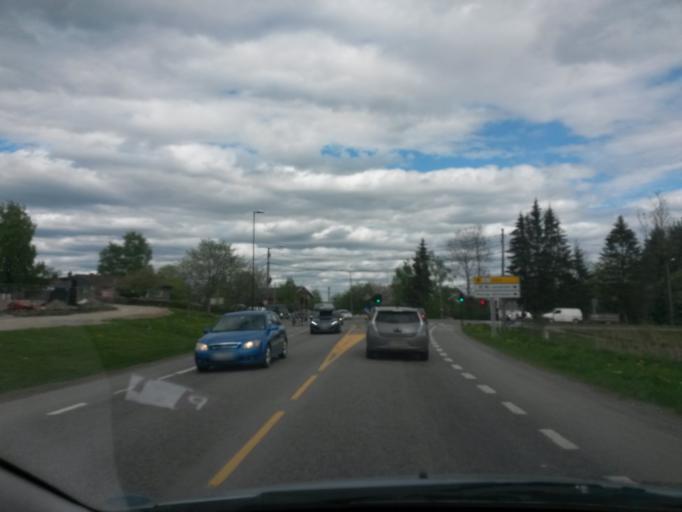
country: NO
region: Akershus
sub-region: Asker
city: Asker
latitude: 59.8296
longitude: 10.4404
